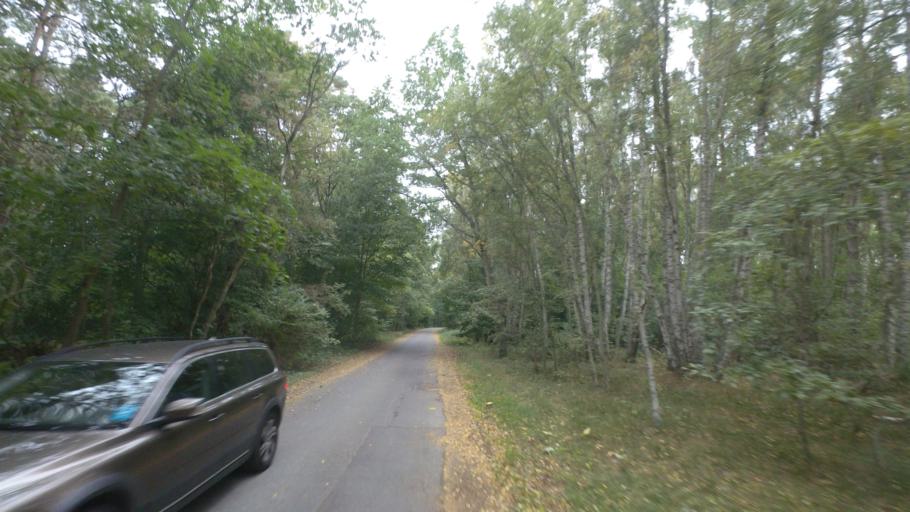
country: DK
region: Capital Region
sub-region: Bornholm Kommune
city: Nexo
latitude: 55.0008
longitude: 15.0385
